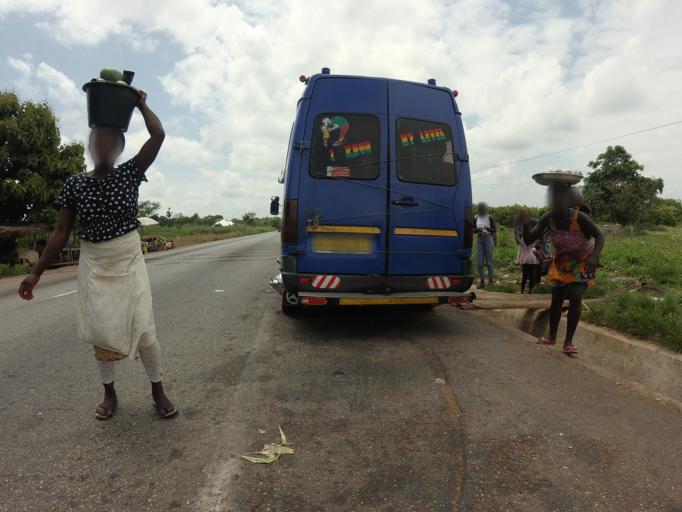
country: GH
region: Brong-Ahafo
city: Techiman
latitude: 7.6527
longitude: -1.8761
